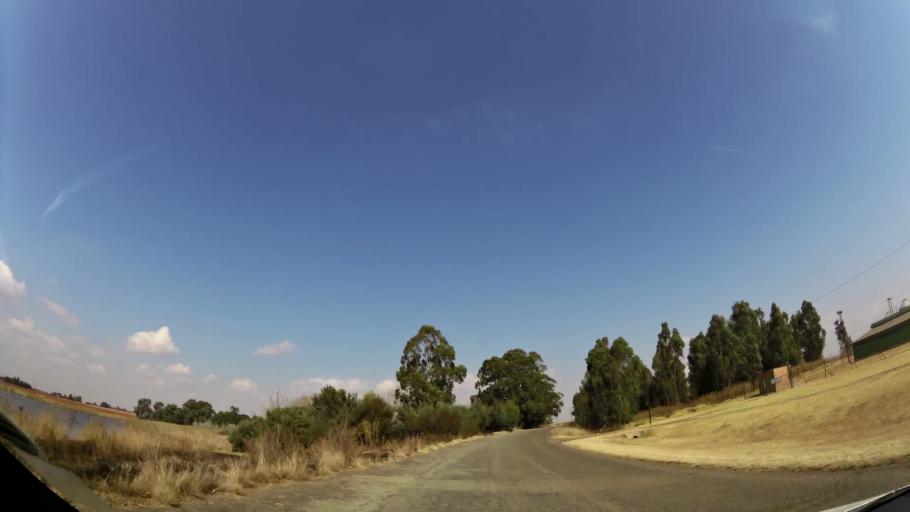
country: ZA
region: Mpumalanga
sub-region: Nkangala District Municipality
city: Delmas
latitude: -26.1513
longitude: 28.5332
